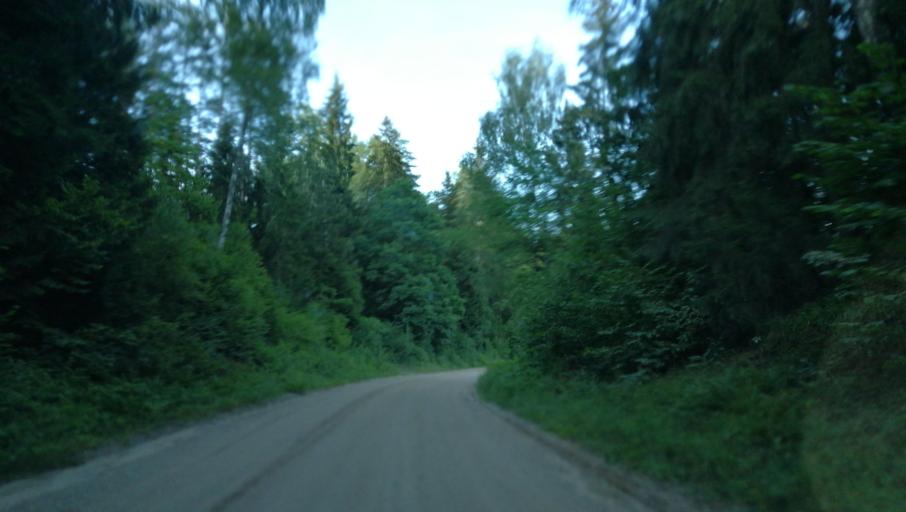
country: LV
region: Cesu Rajons
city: Cesis
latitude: 57.3495
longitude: 25.1927
